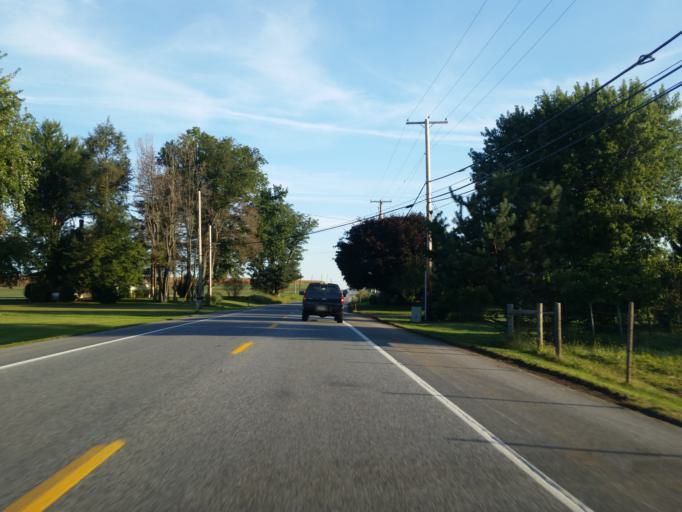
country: US
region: Pennsylvania
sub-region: Lancaster County
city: Quarryville
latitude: 39.7929
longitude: -76.1844
